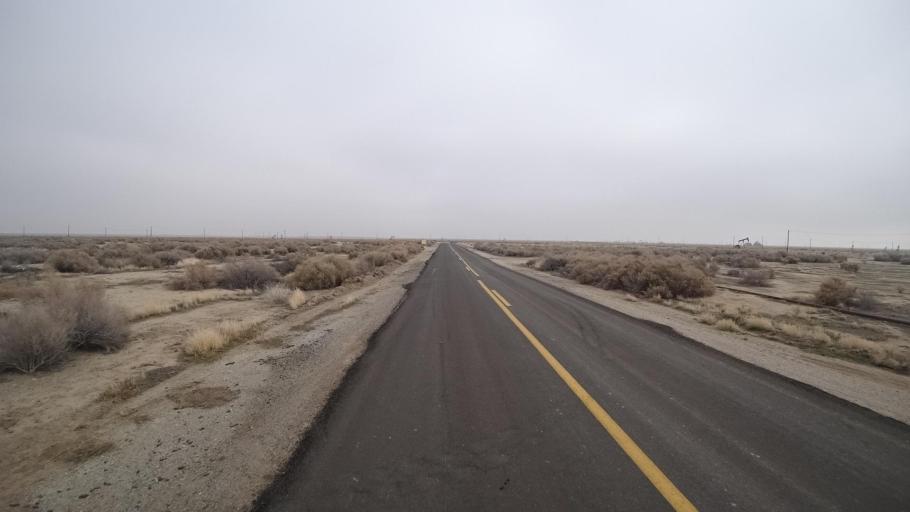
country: US
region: California
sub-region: Kern County
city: Maricopa
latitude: 35.0754
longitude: -119.3553
